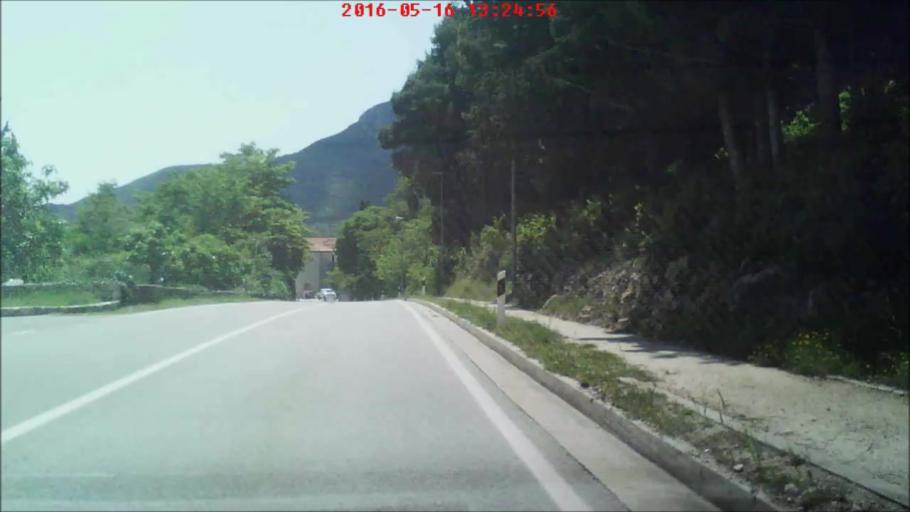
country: HR
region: Dubrovacko-Neretvanska
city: Ston
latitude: 42.8406
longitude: 17.6998
